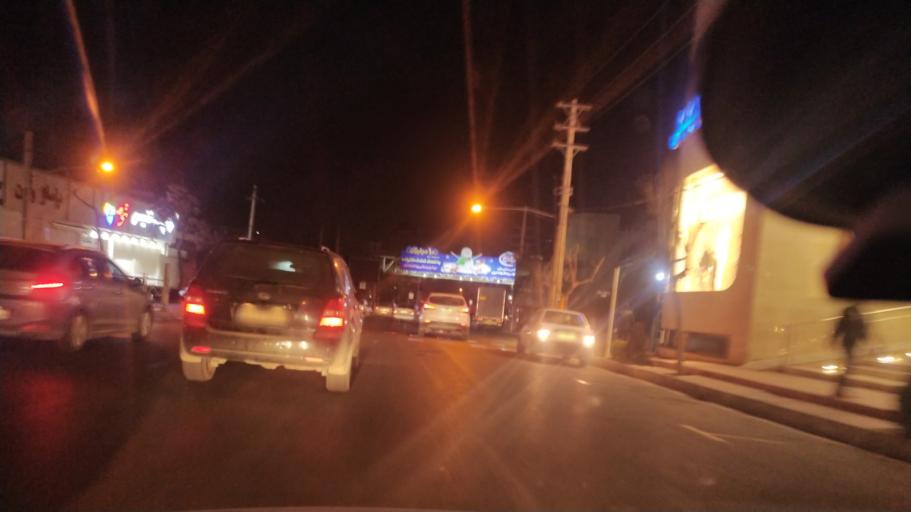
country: IR
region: Alborz
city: Karaj
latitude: 35.8139
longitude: 50.9991
